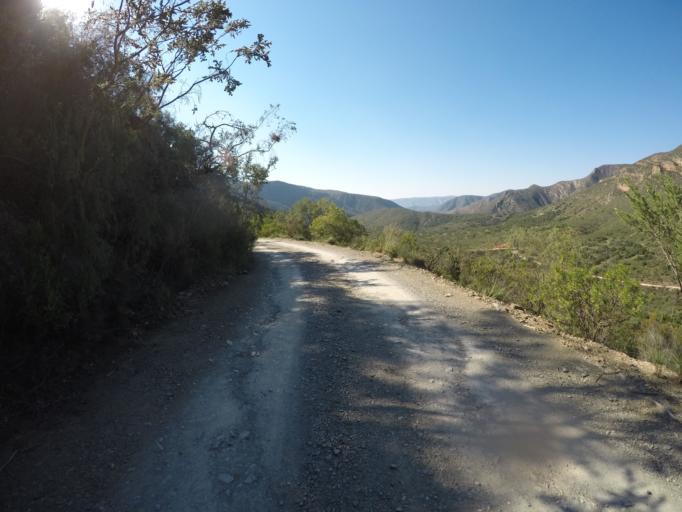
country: ZA
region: Eastern Cape
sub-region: Cacadu District Municipality
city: Kareedouw
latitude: -33.6554
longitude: 24.5063
